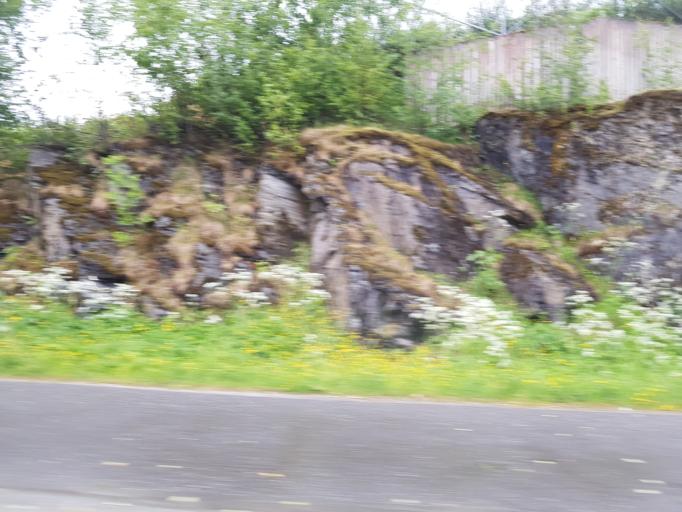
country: NO
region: Sor-Trondelag
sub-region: Selbu
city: Mebonden
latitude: 63.2310
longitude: 11.0353
